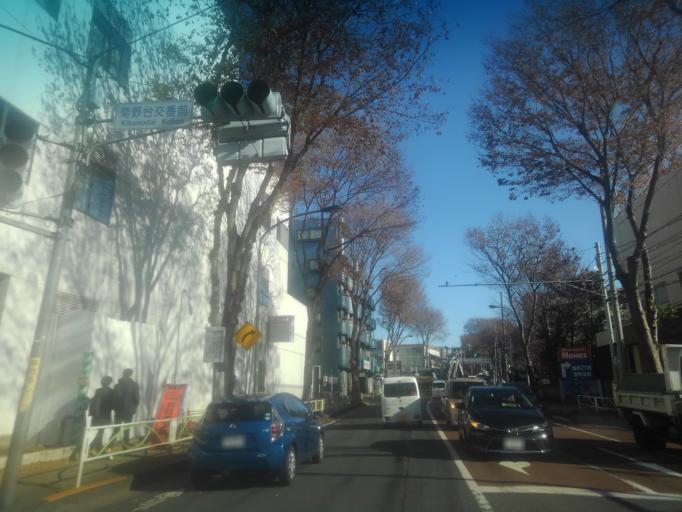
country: JP
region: Tokyo
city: Chofugaoka
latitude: 35.6574
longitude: 139.5693
